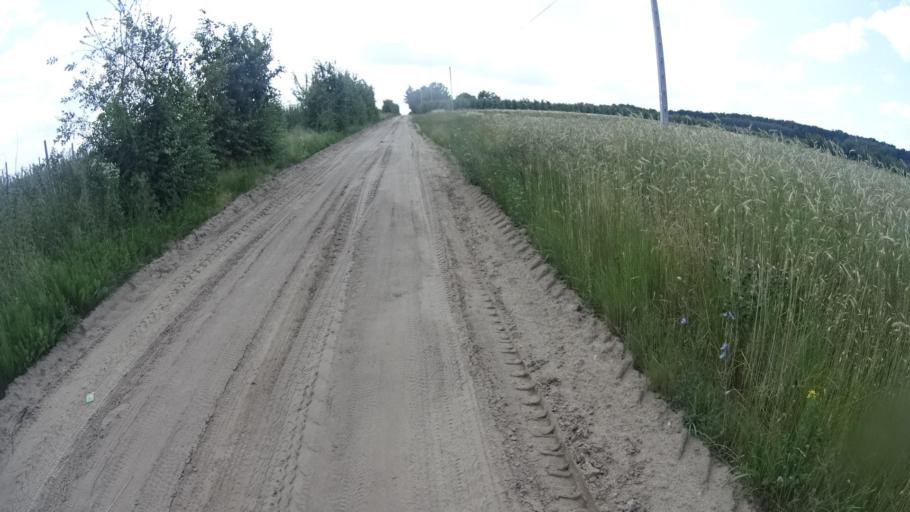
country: PL
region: Masovian Voivodeship
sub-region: Powiat grojecki
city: Goszczyn
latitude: 51.7098
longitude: 20.8303
